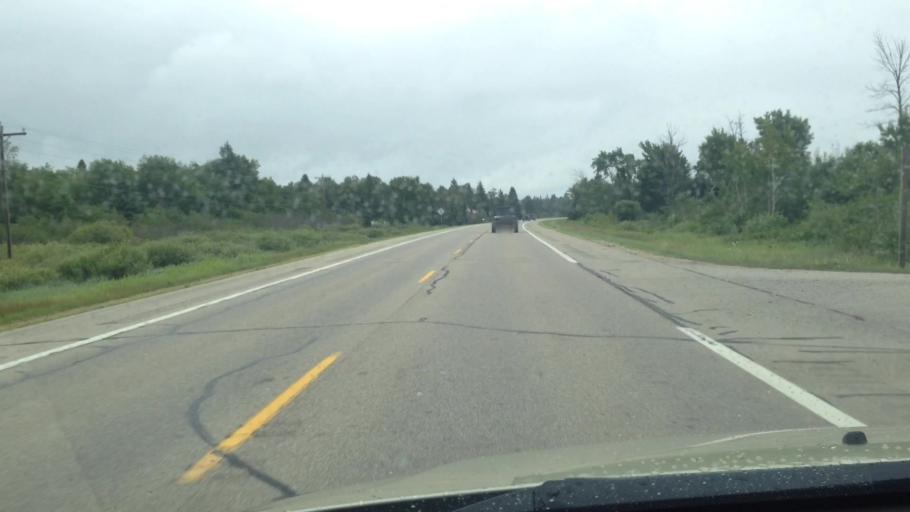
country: US
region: Michigan
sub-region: Schoolcraft County
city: Manistique
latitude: 45.9009
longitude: -86.5657
